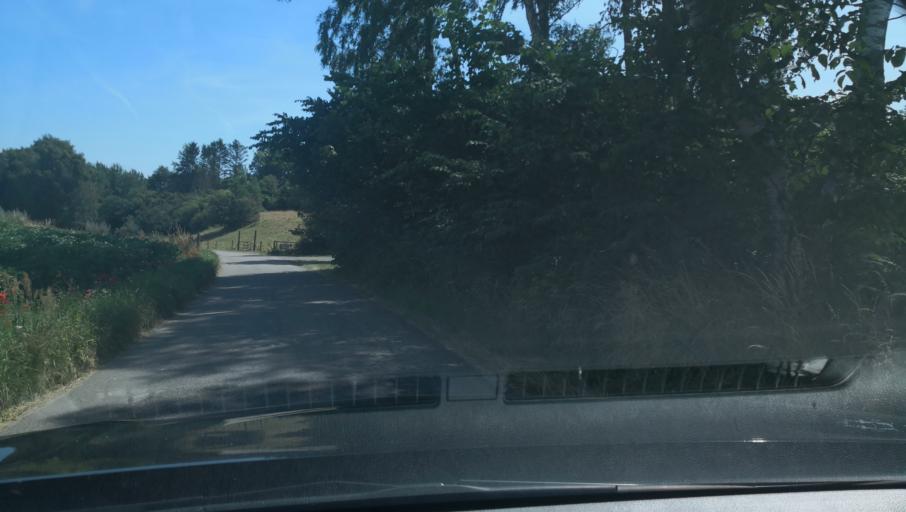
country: SE
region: Skane
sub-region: Ystads Kommun
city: Kopingebro
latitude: 55.3886
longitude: 14.1426
